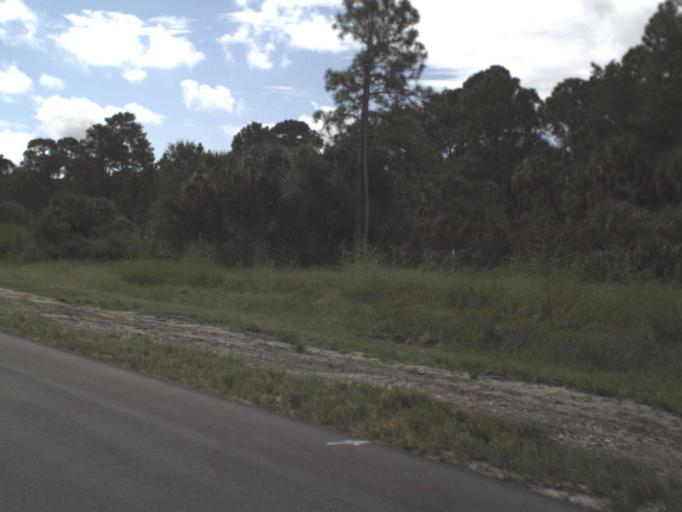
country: US
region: Florida
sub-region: Sarasota County
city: Warm Mineral Springs
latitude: 27.1041
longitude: -82.2957
